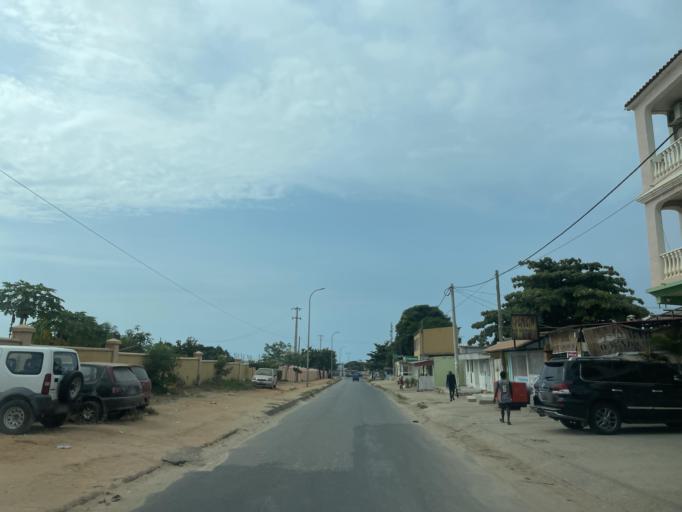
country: AO
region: Luanda
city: Luanda
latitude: -8.9183
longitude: 13.1691
